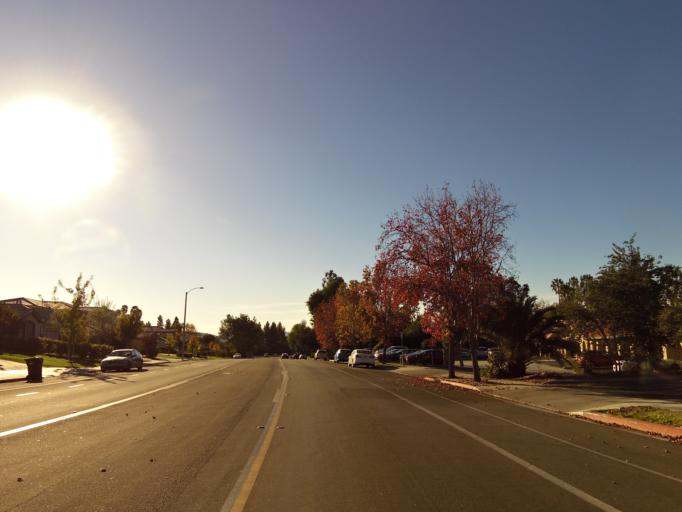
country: US
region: California
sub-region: Ventura County
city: Thousand Oaks
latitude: 34.2187
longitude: -118.8767
